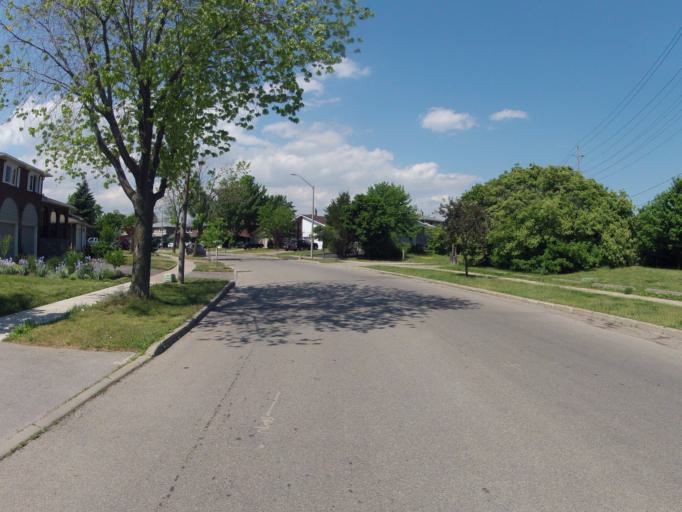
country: CA
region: Ontario
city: Mississauga
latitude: 43.5143
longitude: -79.6531
